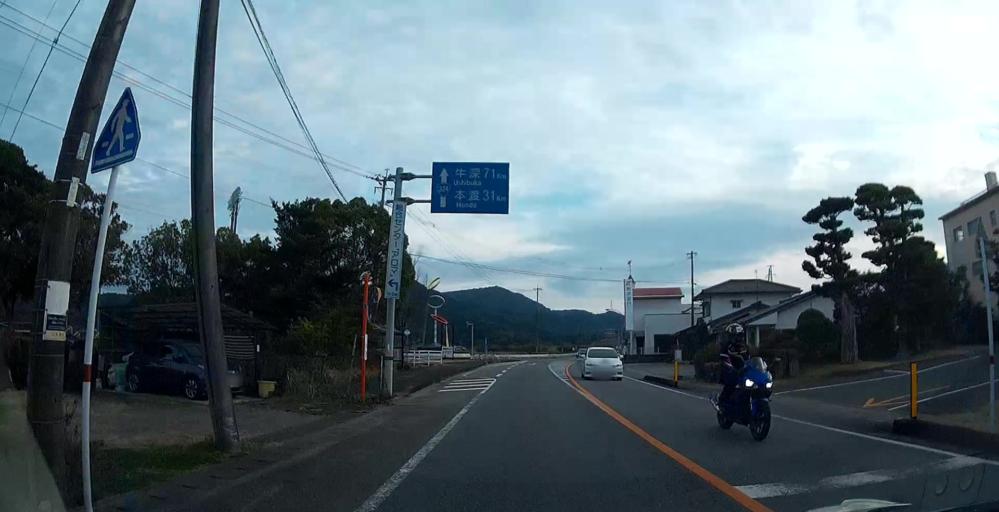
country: JP
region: Kumamoto
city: Yatsushiro
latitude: 32.5147
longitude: 130.4292
